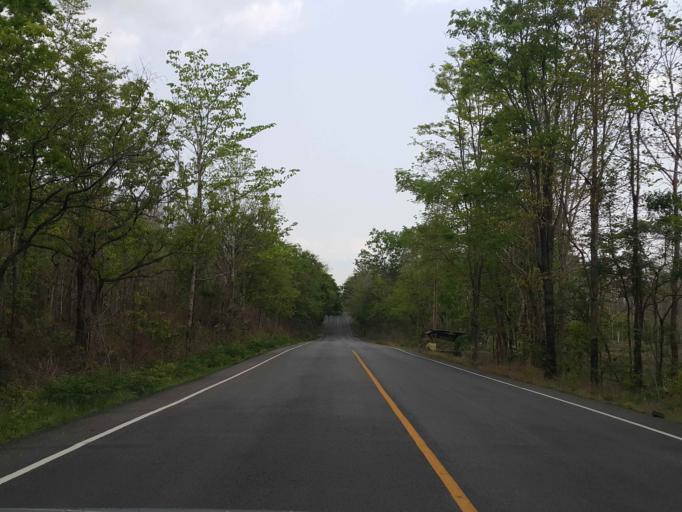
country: TH
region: Sukhothai
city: Thung Saliam
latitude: 17.4142
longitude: 99.3876
